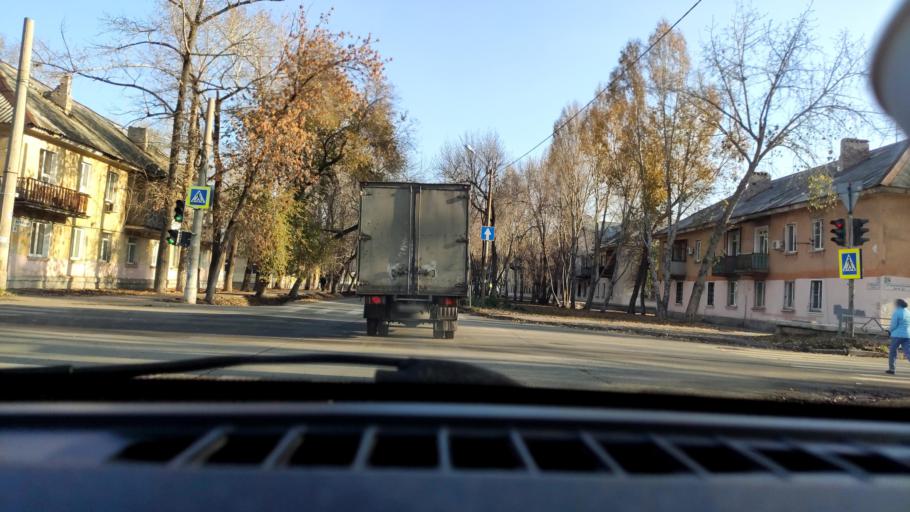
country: RU
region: Samara
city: Samara
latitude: 53.1134
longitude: 50.0725
